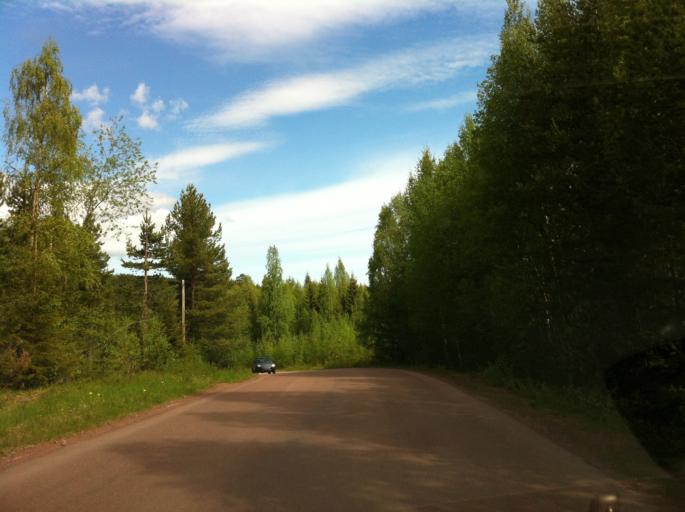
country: SE
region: Dalarna
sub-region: Mora Kommun
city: Mora
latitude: 60.8807
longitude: 14.5180
